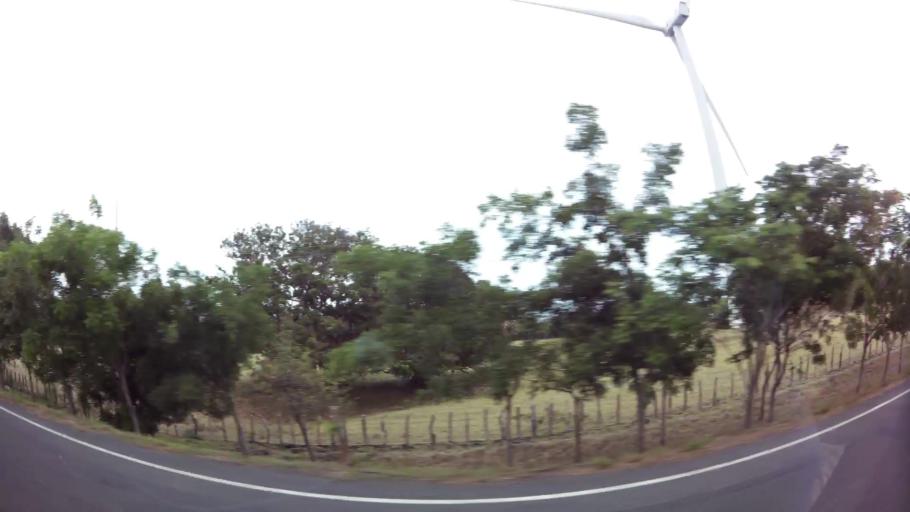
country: NI
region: Rivas
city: Rivas
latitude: 11.3572
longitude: -85.7441
